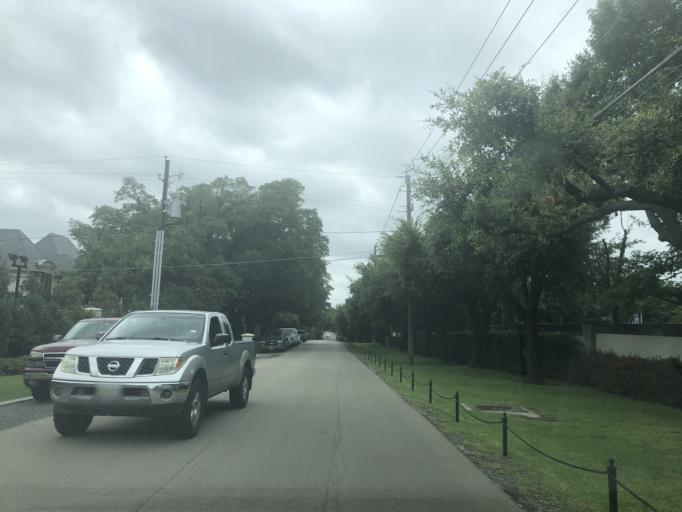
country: US
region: Texas
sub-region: Dallas County
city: University Park
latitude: 32.8706
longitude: -96.8140
